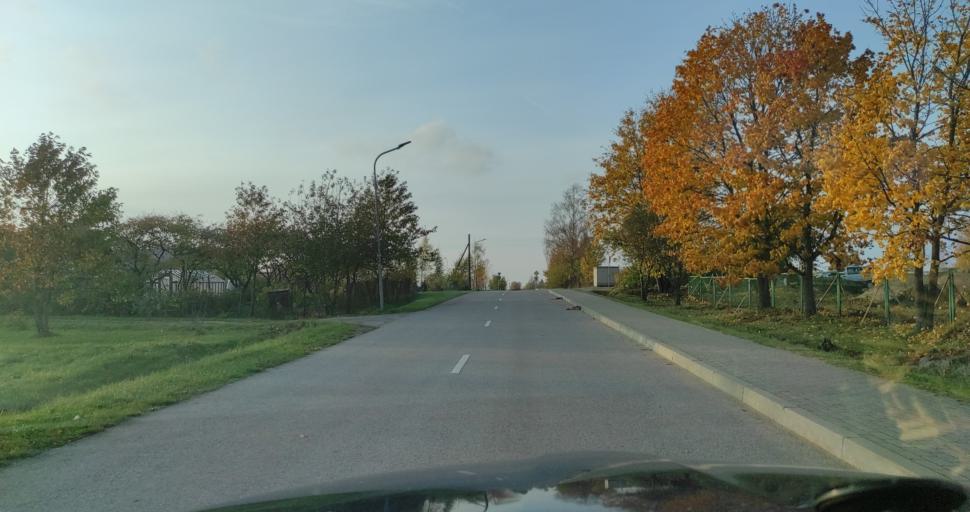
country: LV
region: Vainode
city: Vainode
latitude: 56.4205
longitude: 21.8514
